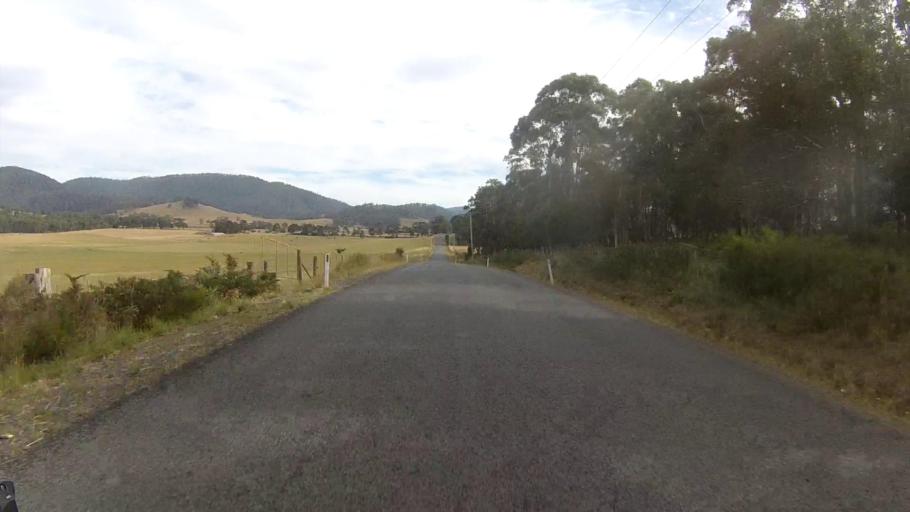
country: AU
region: Tasmania
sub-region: Sorell
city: Sorell
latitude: -42.8012
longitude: 147.7935
